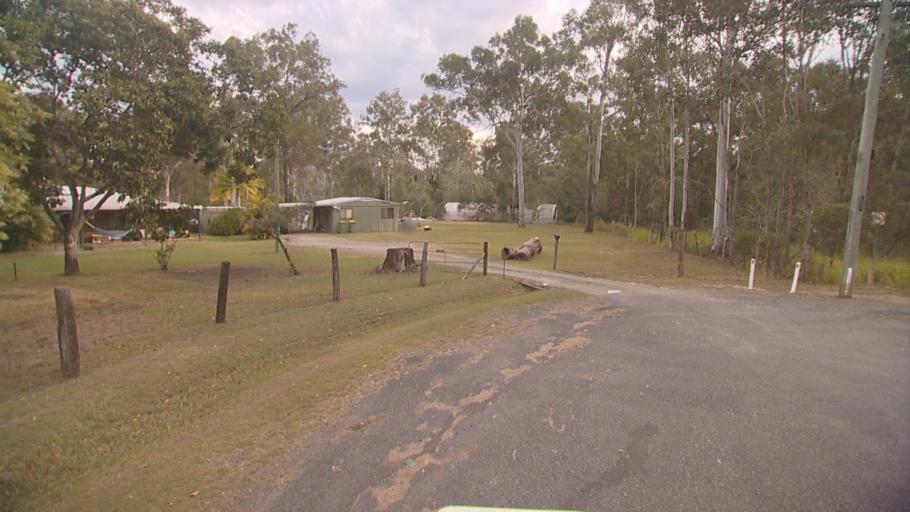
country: AU
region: Queensland
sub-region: Logan
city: Chambers Flat
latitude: -27.7750
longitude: 153.1126
